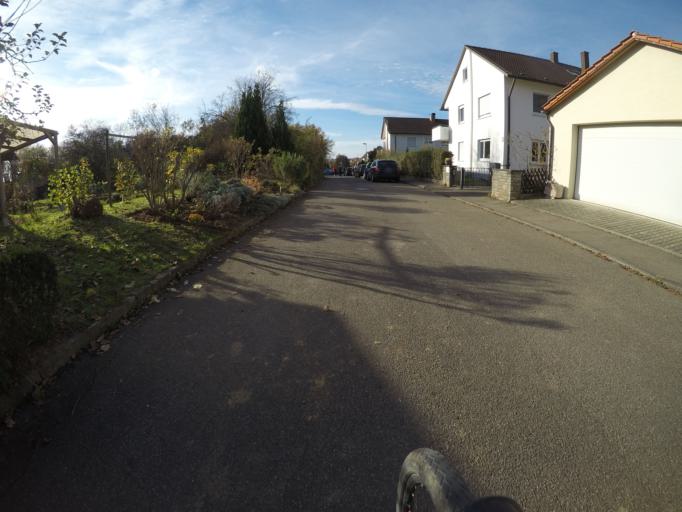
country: DE
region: Baden-Wuerttemberg
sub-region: Regierungsbezirk Stuttgart
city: Weinstadt-Endersbach
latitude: 48.8075
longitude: 9.3658
